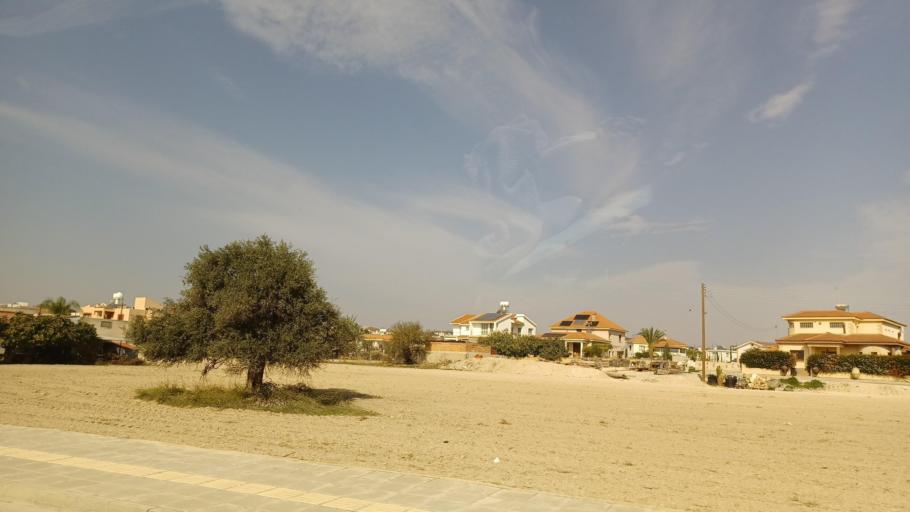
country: CY
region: Lefkosia
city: Lympia
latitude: 34.9947
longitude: 33.4701
